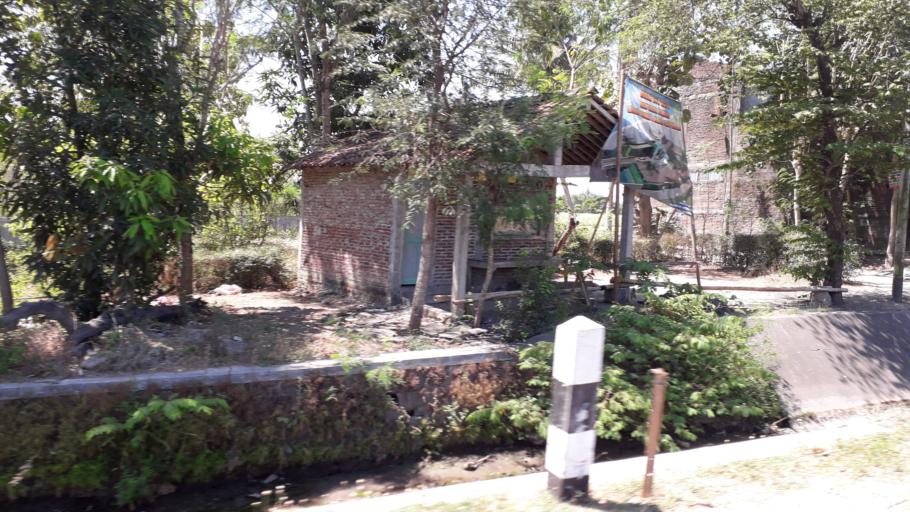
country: ID
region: Daerah Istimewa Yogyakarta
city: Pundong
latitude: -7.9423
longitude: 110.3335
